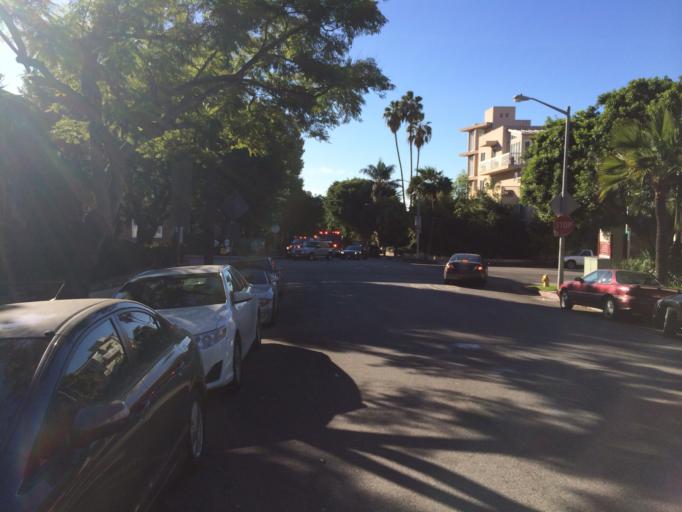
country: US
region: California
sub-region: Los Angeles County
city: West Hollywood
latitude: 34.0948
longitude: -118.3674
